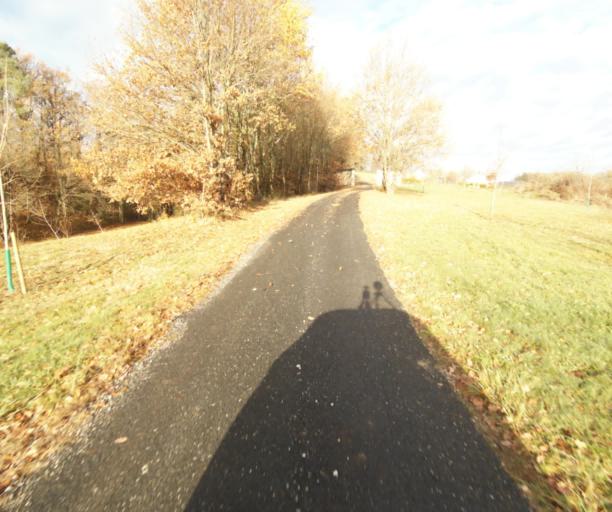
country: FR
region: Limousin
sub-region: Departement de la Correze
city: Saint-Mexant
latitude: 45.2546
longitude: 1.6382
